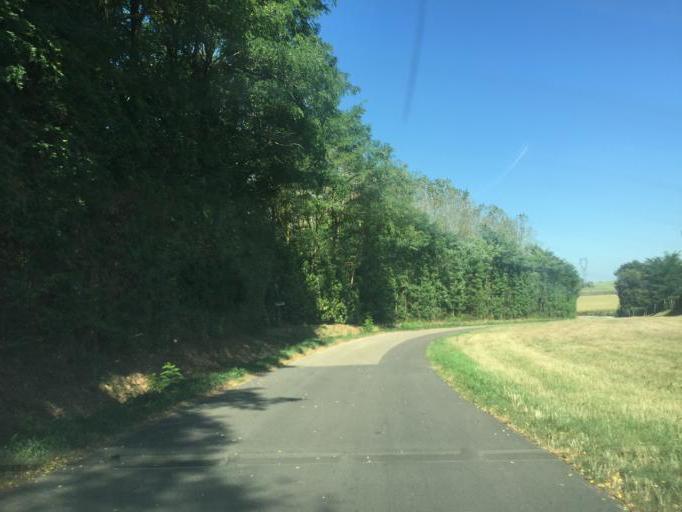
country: FR
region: Rhone-Alpes
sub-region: Departement de l'Ain
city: Saint-Maurice-de-Beynost
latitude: 45.8531
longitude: 4.9743
